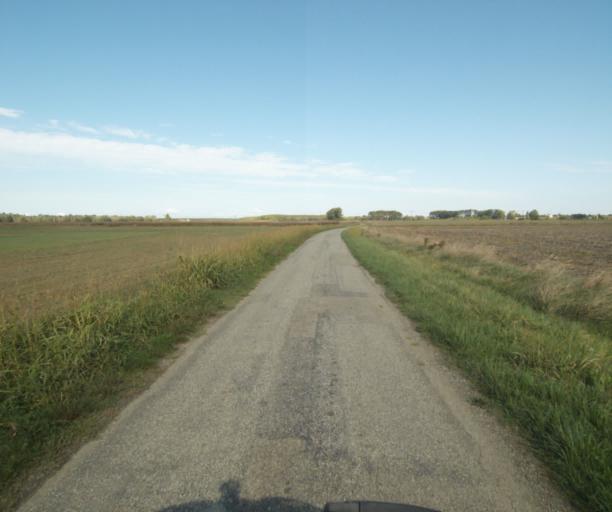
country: FR
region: Midi-Pyrenees
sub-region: Departement du Tarn-et-Garonne
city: Finhan
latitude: 43.8884
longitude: 1.2208
